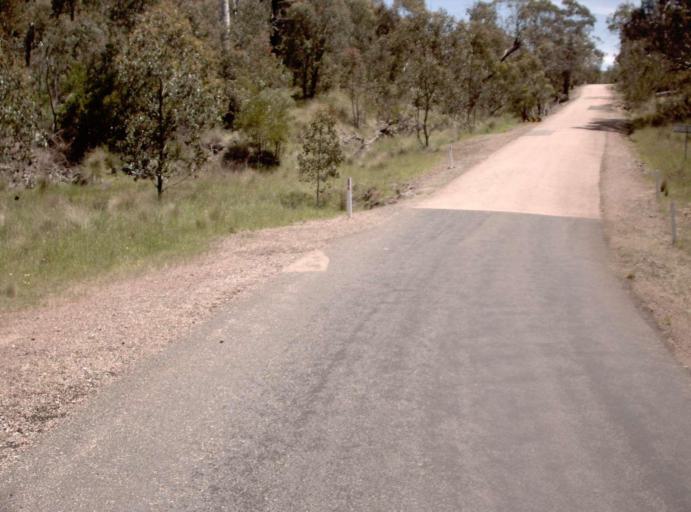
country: AU
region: New South Wales
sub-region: Snowy River
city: Jindabyne
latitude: -37.1066
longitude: 148.2500
